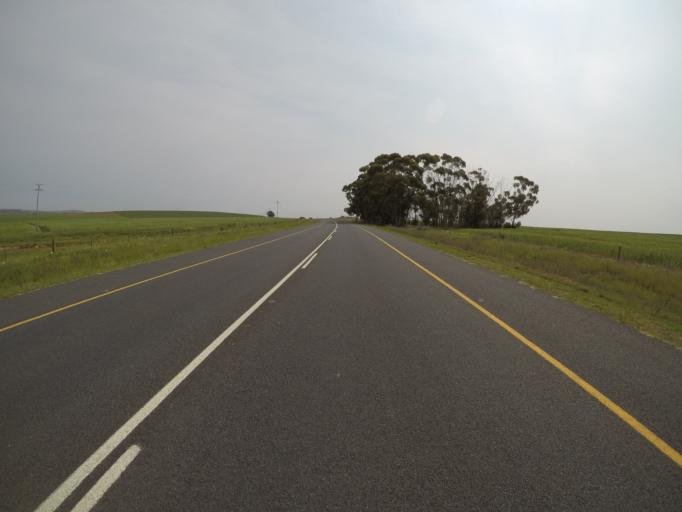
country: ZA
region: Western Cape
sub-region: West Coast District Municipality
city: Malmesbury
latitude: -33.5120
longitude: 18.8450
